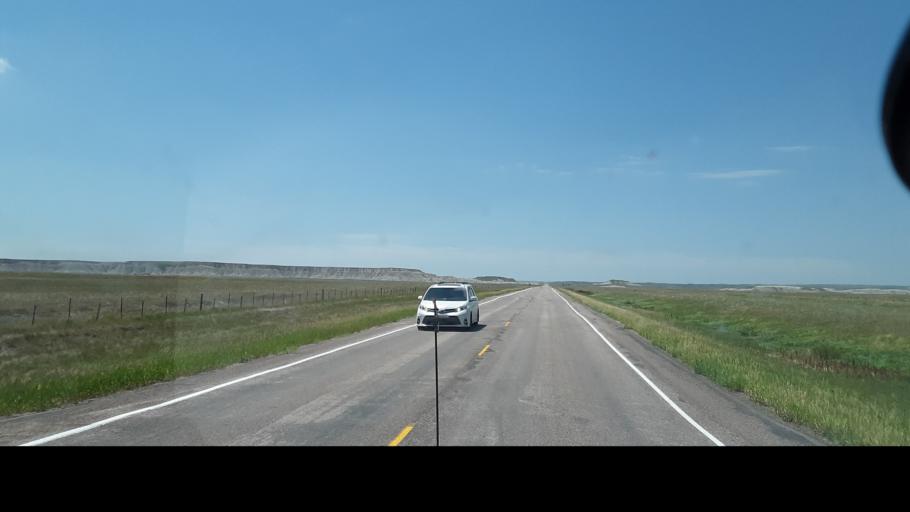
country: US
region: South Dakota
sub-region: Shannon County
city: Porcupine
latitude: 43.7170
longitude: -102.2850
